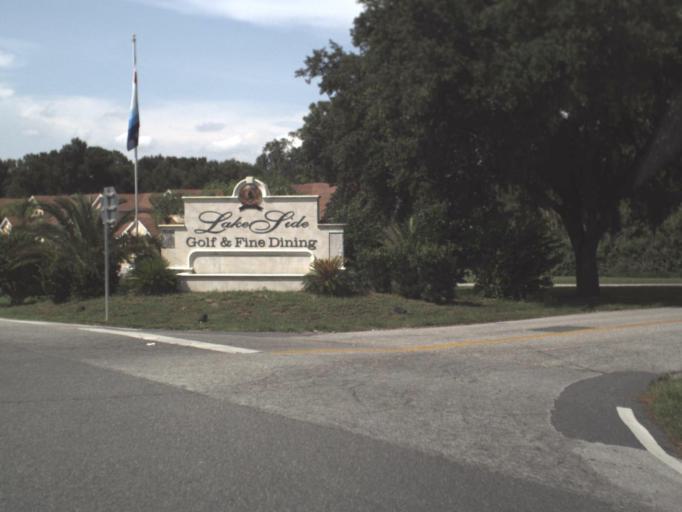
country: US
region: Florida
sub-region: Citrus County
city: Inverness Highlands North
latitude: 28.8741
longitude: -82.3622
